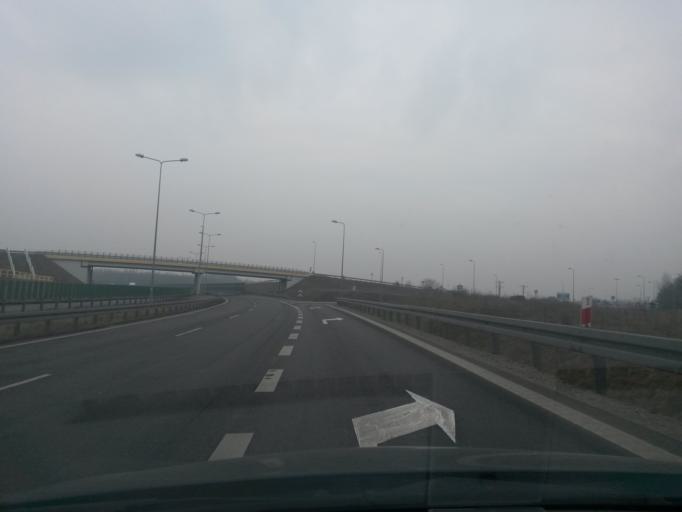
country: PL
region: Masovian Voivodeship
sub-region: Powiat legionowski
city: Serock
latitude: 52.4922
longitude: 21.0495
